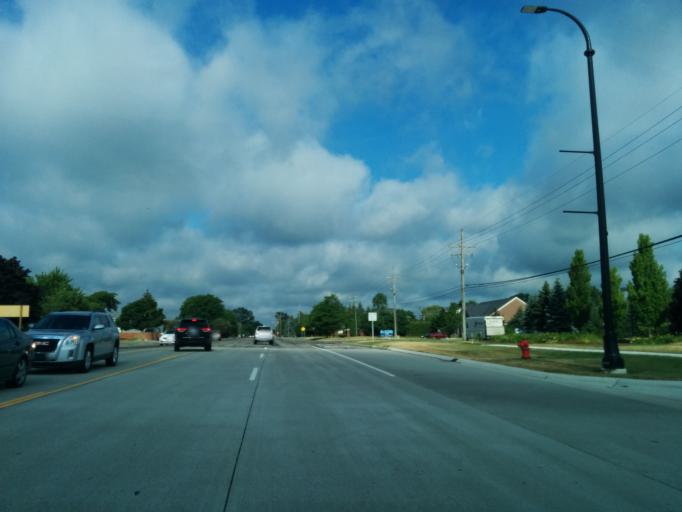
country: US
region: Michigan
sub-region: Oakland County
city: Farmington Hills
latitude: 42.5284
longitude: -83.3627
